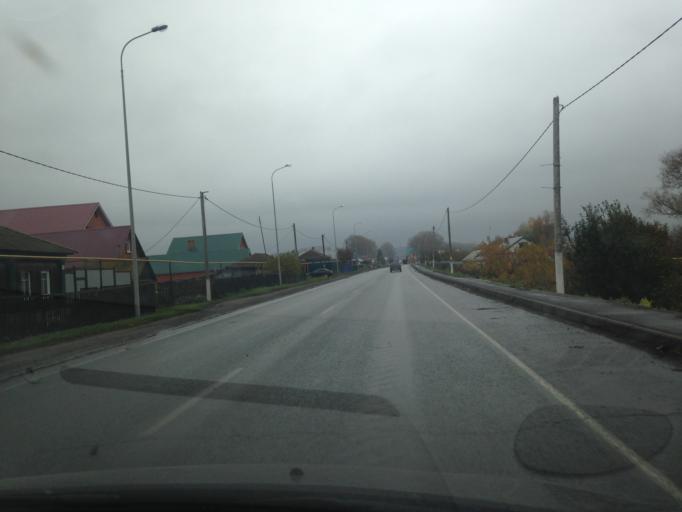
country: RU
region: Tatarstan
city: Buinsk
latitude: 54.9951
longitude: 48.3328
